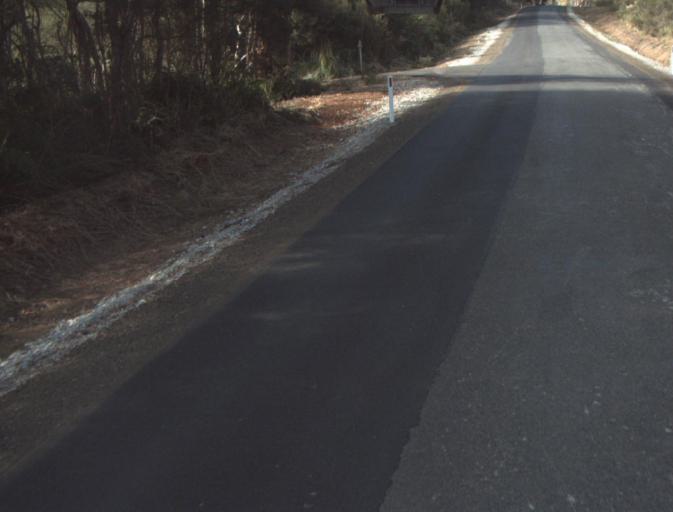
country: AU
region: Tasmania
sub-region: Launceston
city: Mayfield
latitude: -41.3086
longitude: 147.1988
